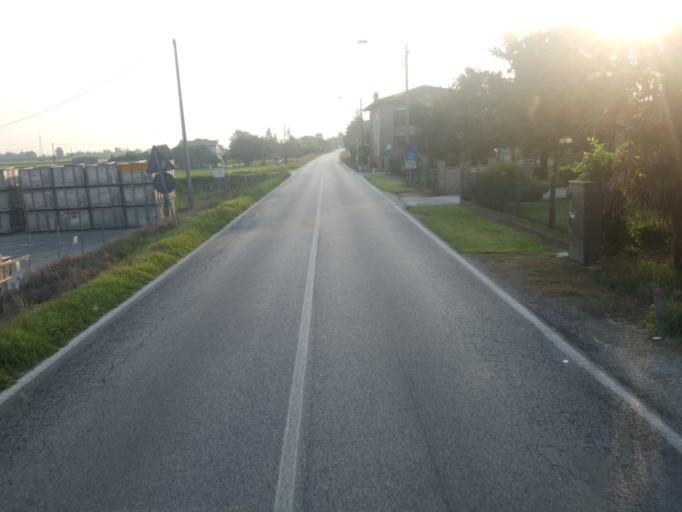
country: IT
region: Emilia-Romagna
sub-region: Provincia di Ravenna
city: Voltana
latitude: 44.5894
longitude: 11.9380
